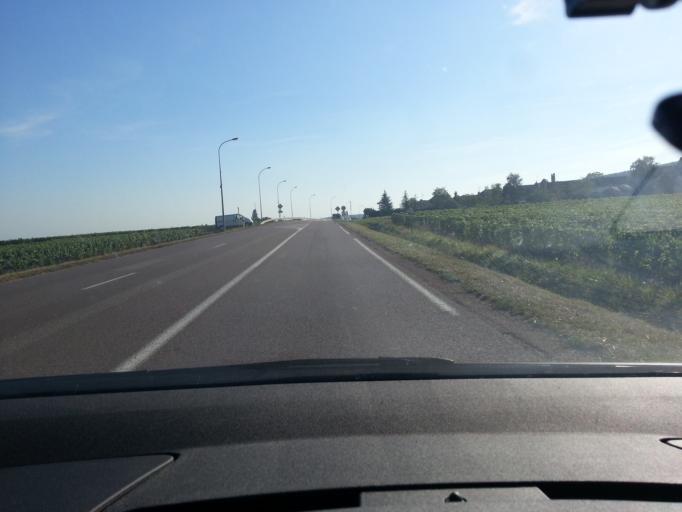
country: FR
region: Bourgogne
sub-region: Departement de la Cote-d'Or
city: Beaune
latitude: 47.0795
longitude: 4.8893
